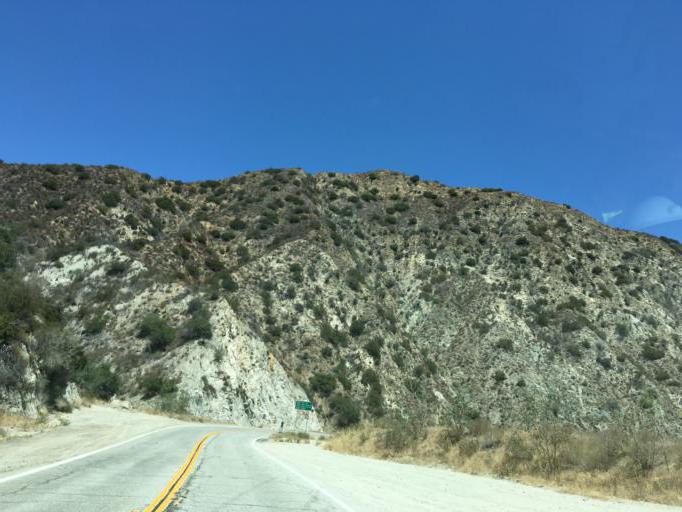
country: US
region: California
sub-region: Los Angeles County
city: La Crescenta-Montrose
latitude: 34.3035
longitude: -118.2640
